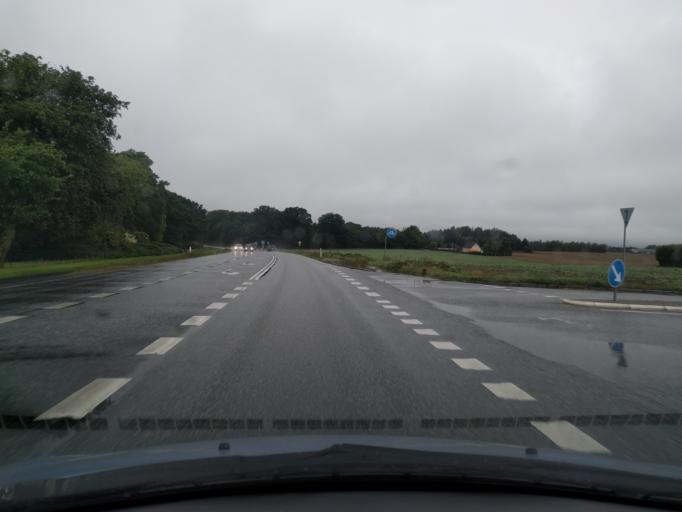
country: DK
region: Zealand
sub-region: Naestved Kommune
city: Fuglebjerg
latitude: 55.2777
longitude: 11.6198
